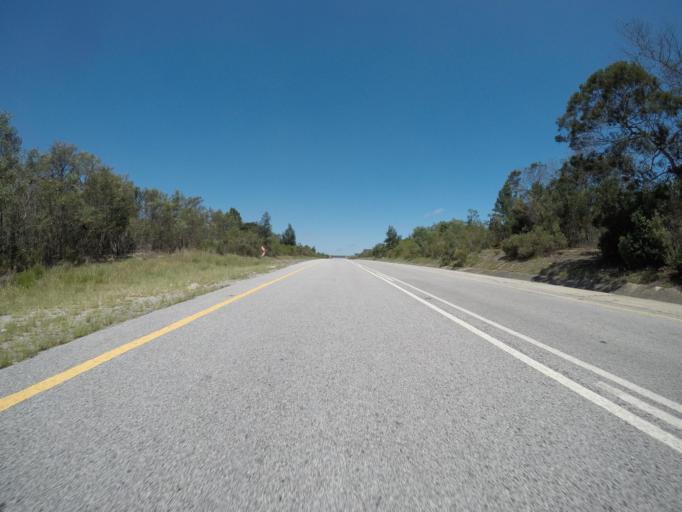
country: ZA
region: Eastern Cape
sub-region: Cacadu District Municipality
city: Kruisfontein
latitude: -34.0267
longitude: 24.5980
